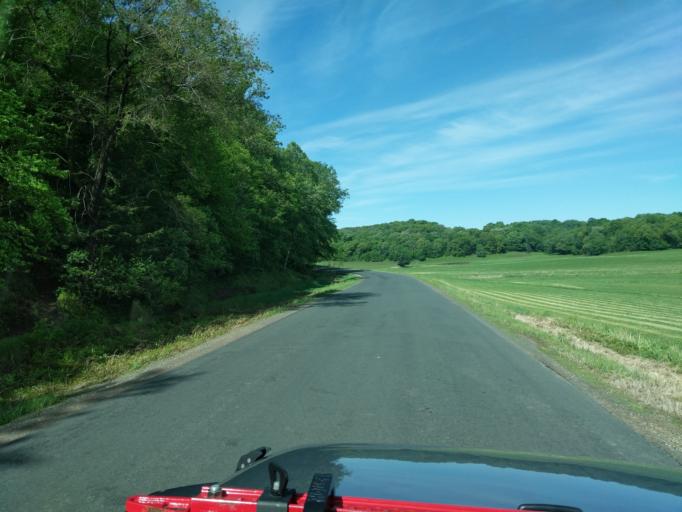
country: US
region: Wisconsin
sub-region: Pierce County
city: River Falls
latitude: 44.8632
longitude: -92.5218
